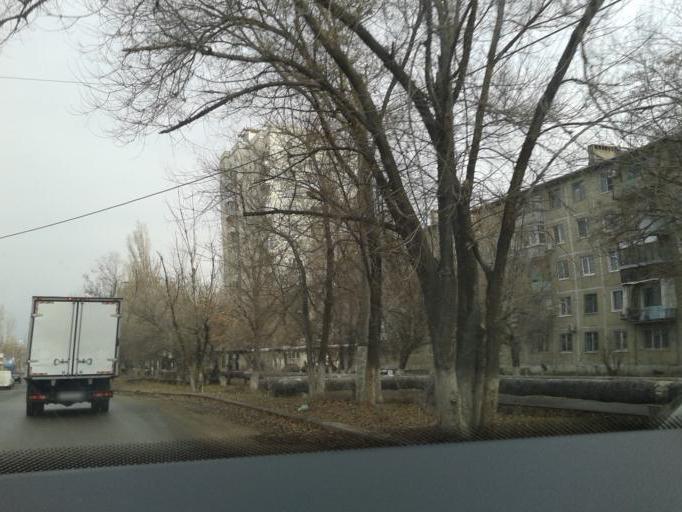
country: RU
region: Volgograd
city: Gorodishche
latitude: 48.7599
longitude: 44.4788
